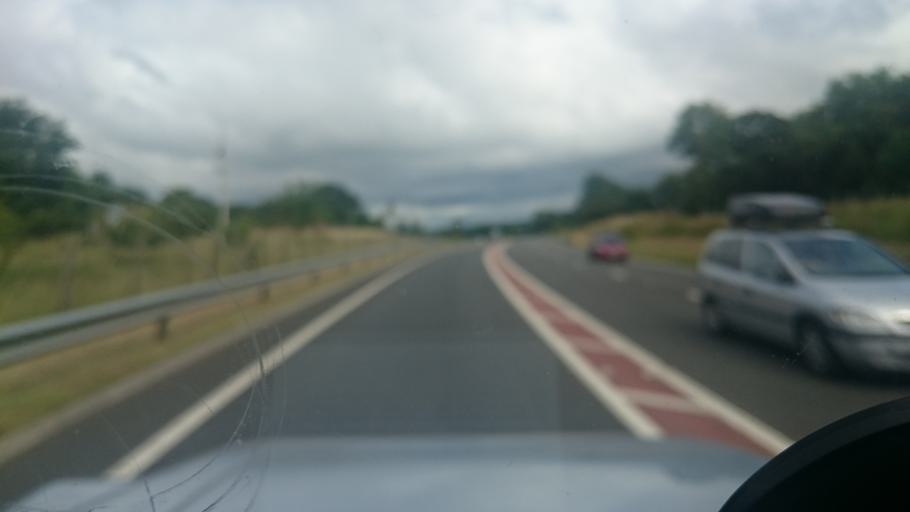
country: GB
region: Wales
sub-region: Pembrokeshire
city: Wiston
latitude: 51.8023
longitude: -4.8088
